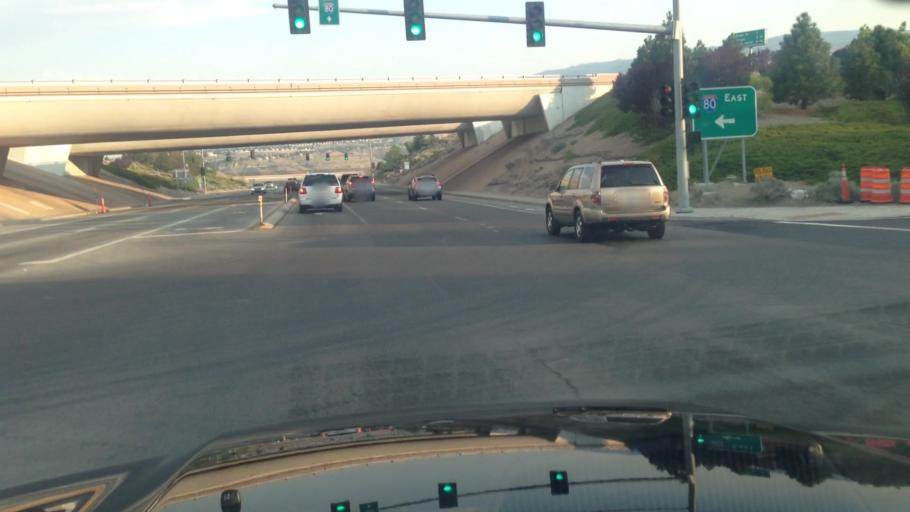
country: US
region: Nevada
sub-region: Washoe County
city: Reno
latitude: 39.5251
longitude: -119.8626
